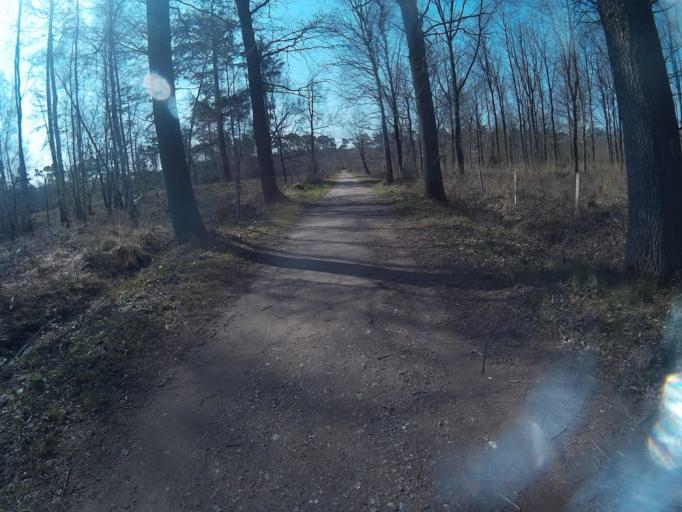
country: BE
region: Flanders
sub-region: Provincie Oost-Vlaanderen
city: Knesselare
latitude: 51.1572
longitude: 3.4574
